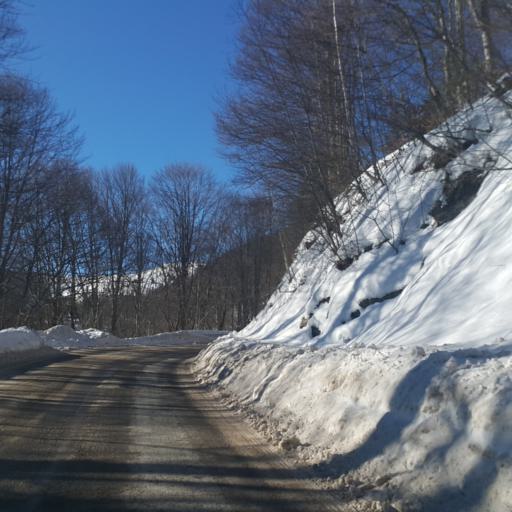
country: XK
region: Mitrovica
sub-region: Komuna e Leposaviqit
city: Leposaviq
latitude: 43.3139
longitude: 20.8534
